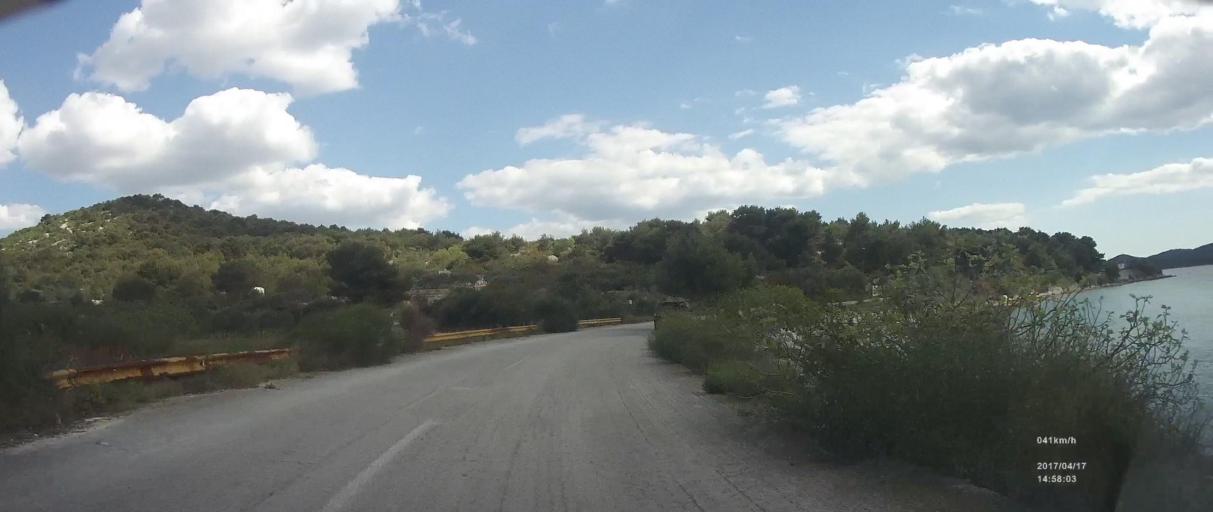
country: HR
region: Sibensko-Kniniska
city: Murter
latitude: 43.8408
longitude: 15.6276
